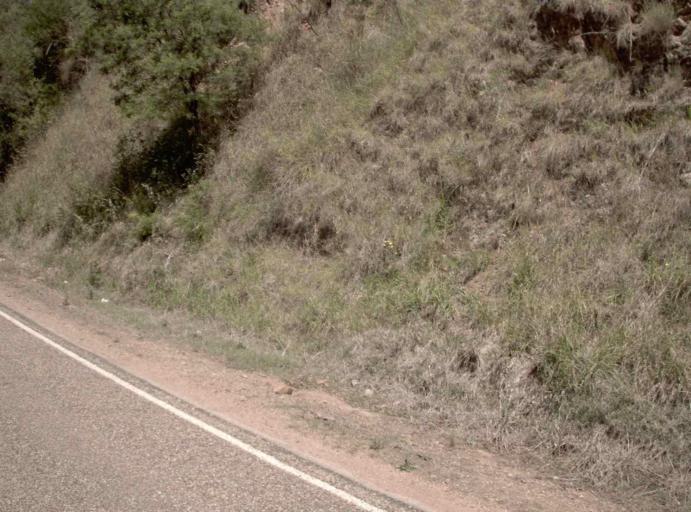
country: AU
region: Victoria
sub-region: East Gippsland
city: Bairnsdale
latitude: -37.3846
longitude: 147.8302
